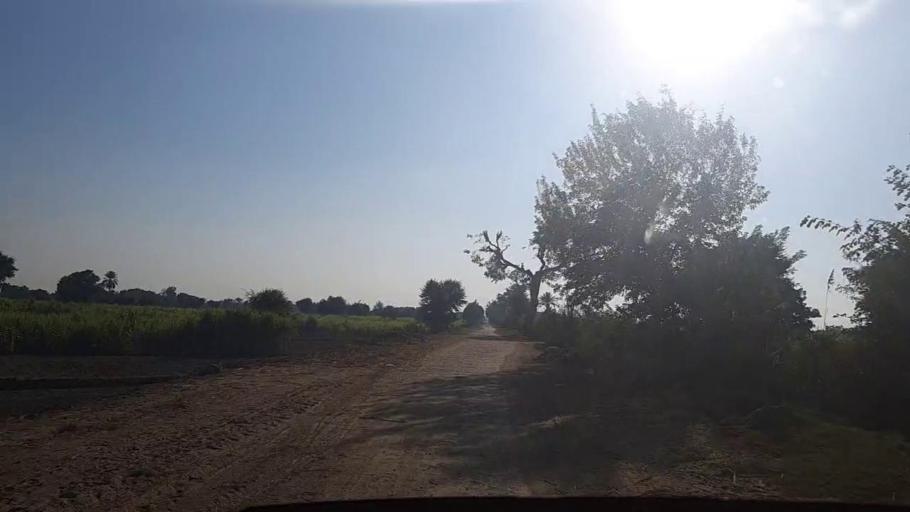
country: PK
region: Sindh
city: Gambat
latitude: 27.3535
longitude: 68.4531
